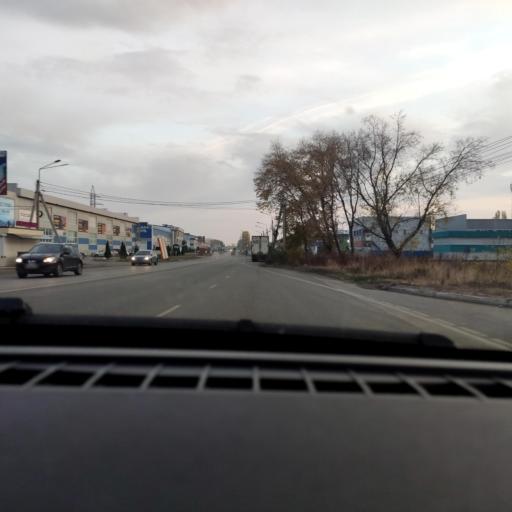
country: RU
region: Voronezj
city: Maslovka
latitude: 51.6351
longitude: 39.2906
